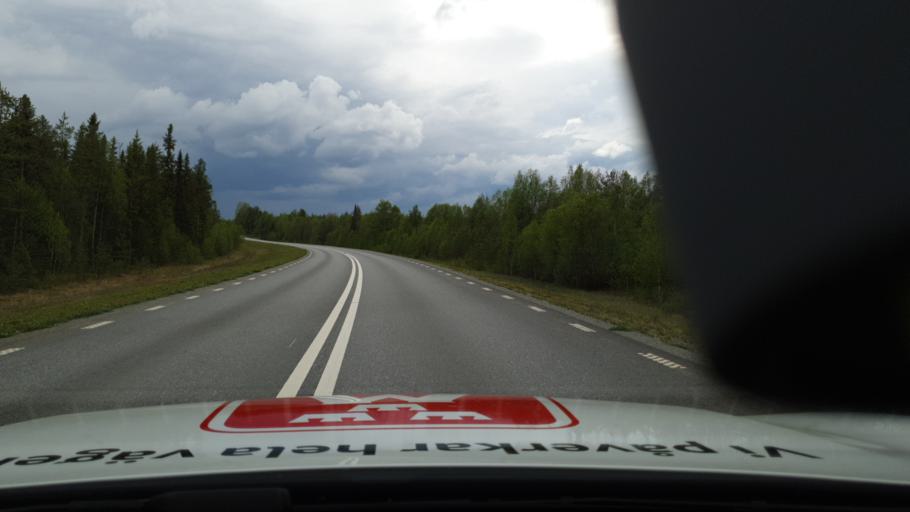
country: SE
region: Vaesterbotten
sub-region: Dorotea Kommun
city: Dorotea
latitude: 64.2829
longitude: 16.5046
